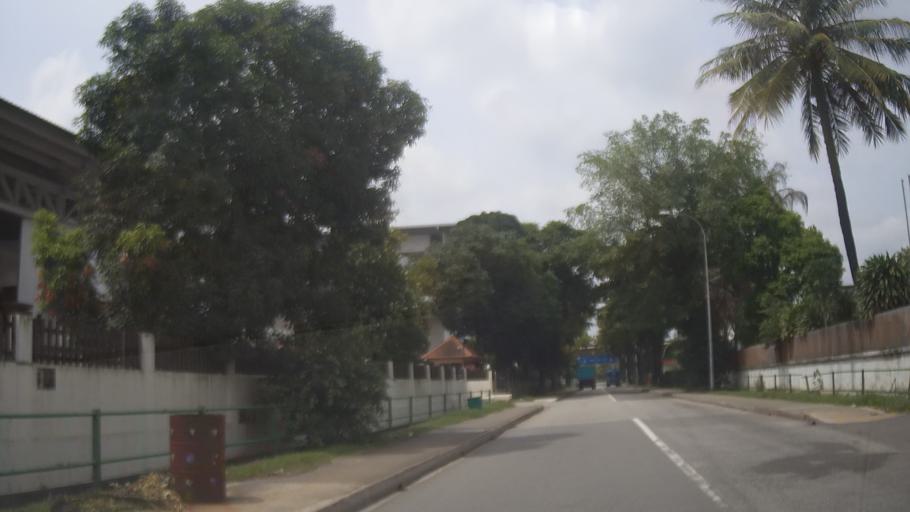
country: MY
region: Johor
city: Johor Bahru
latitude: 1.4147
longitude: 103.7506
